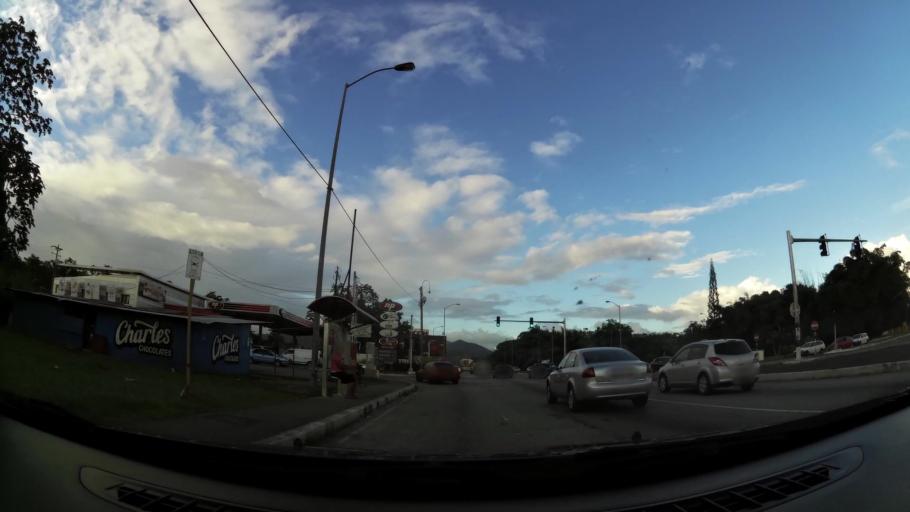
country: TT
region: Tunapuna/Piarco
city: Arouca
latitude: 10.6108
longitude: -61.3443
